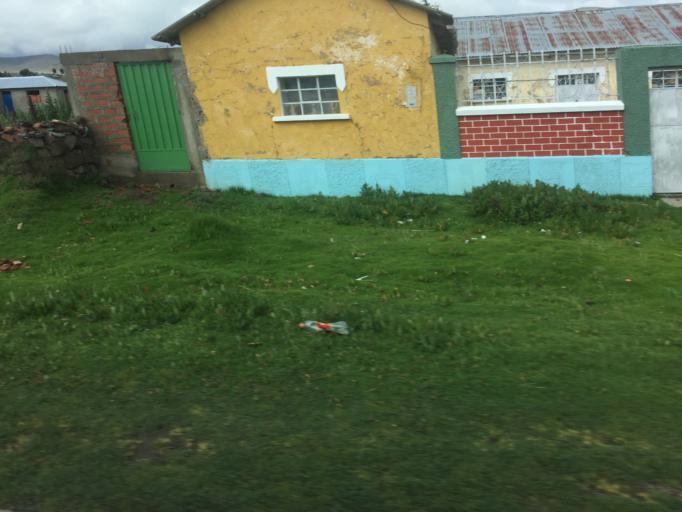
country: PE
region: Puno
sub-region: Provincia de Chucuito
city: Juli
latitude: -16.2220
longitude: -69.3898
